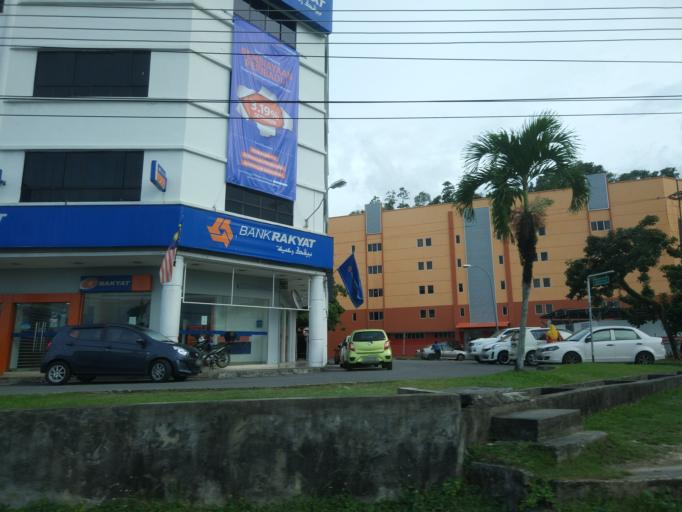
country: MY
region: Sabah
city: Kota Kinabalu
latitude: 5.9922
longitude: 116.1108
